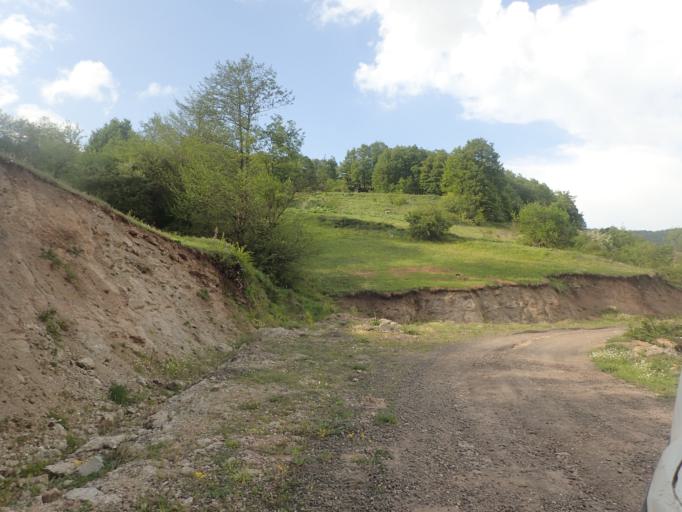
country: TR
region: Ordu
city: Akkus
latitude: 40.8186
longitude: 36.9384
